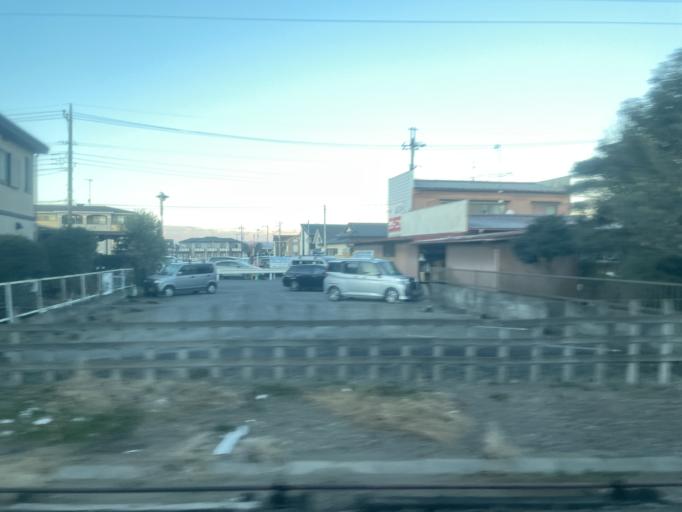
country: JP
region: Saitama
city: Fukayacho
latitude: 36.2064
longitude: 139.2363
